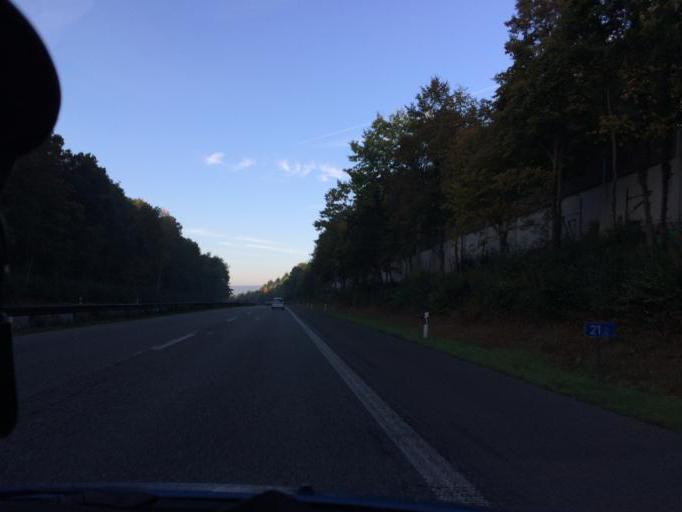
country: DE
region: North Rhine-Westphalia
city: Meckenheim
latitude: 50.6217
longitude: 7.0534
